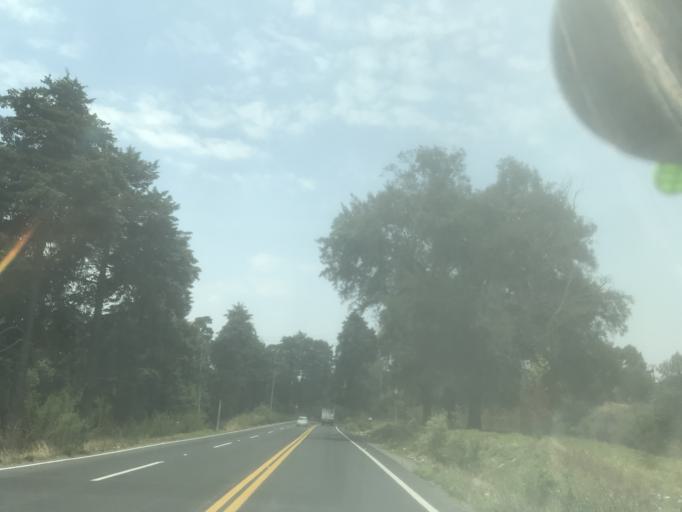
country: MX
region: Mexico
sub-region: Amecameca
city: San Diego Huehuecalco
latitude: 19.0765
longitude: -98.7814
